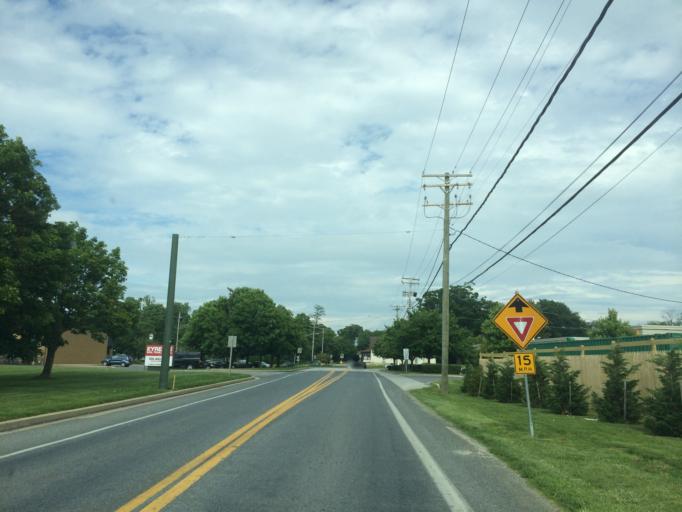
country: US
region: Maryland
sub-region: Howard County
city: Highland
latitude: 39.2637
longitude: -76.9879
